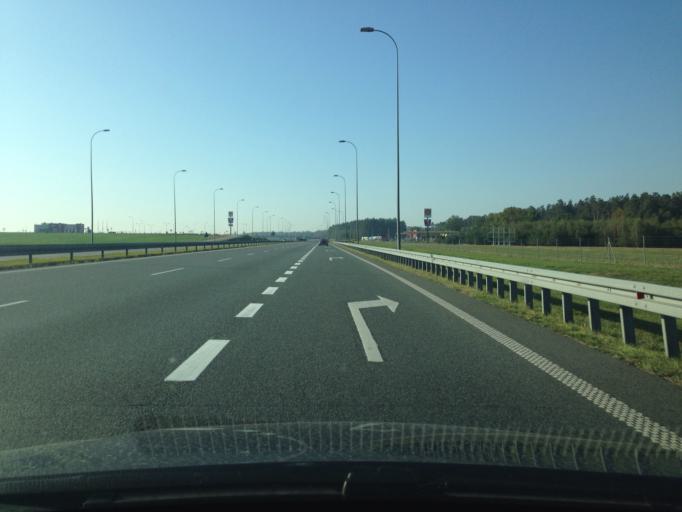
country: PL
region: Pomeranian Voivodeship
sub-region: Powiat tczewski
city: Pelplin
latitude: 53.8918
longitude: 18.6333
